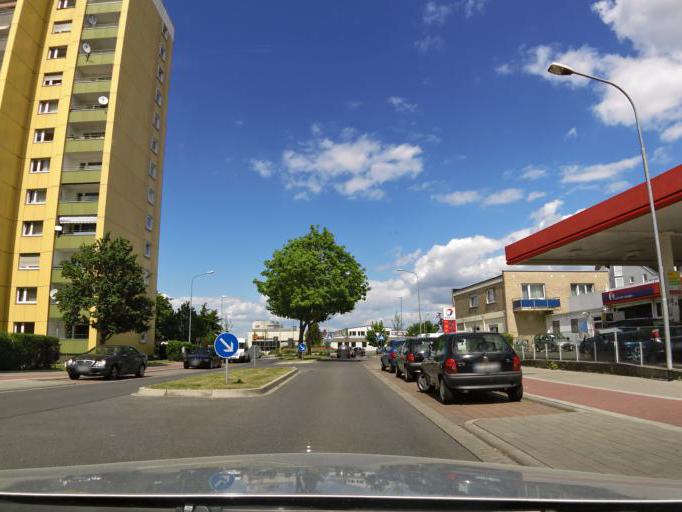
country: DE
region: Hesse
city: Langen
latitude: 49.9922
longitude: 8.6492
